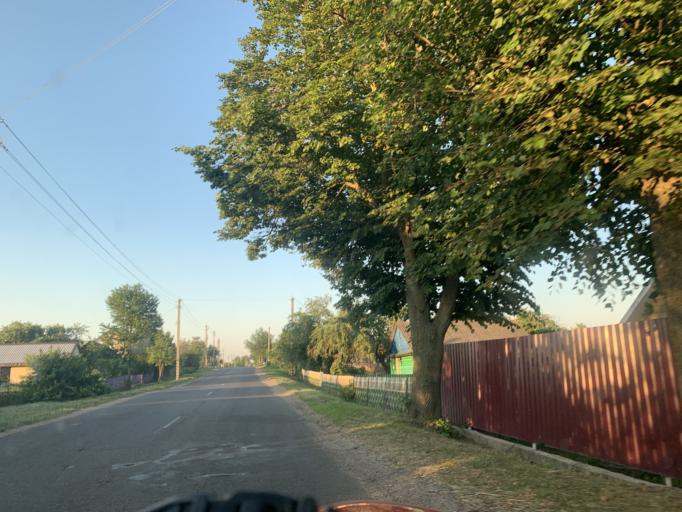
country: BY
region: Minsk
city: Haradzyeya
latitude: 53.2459
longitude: 26.5096
